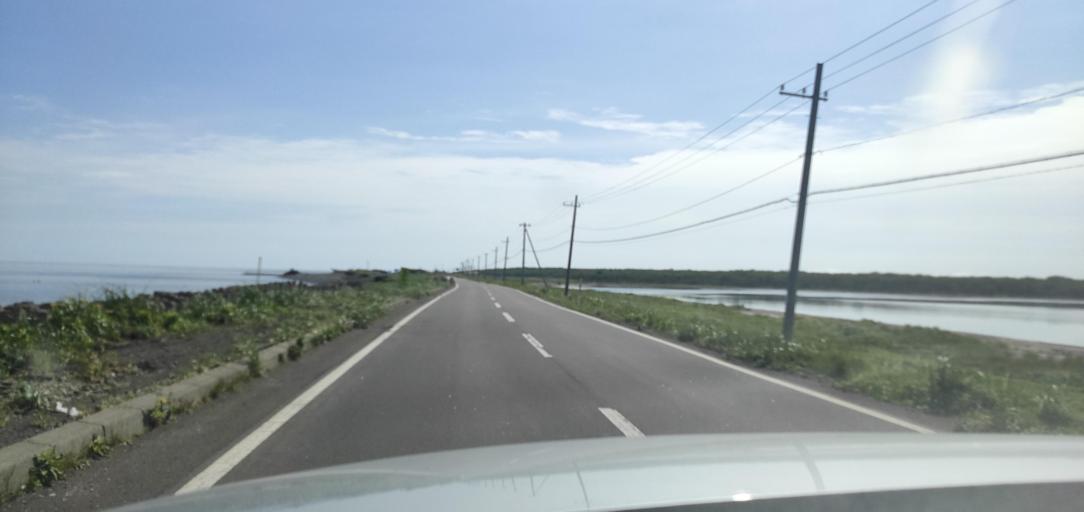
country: JP
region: Hokkaido
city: Shibetsu
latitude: 43.6119
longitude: 145.2628
